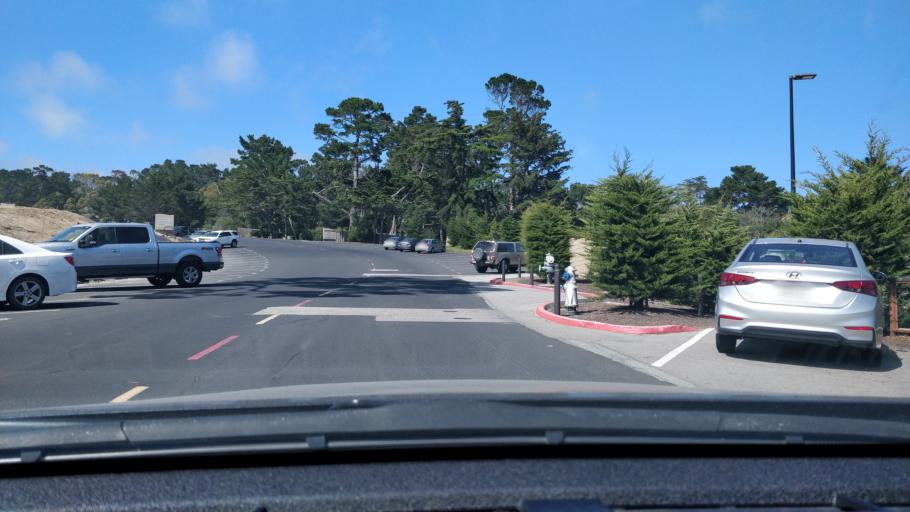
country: US
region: California
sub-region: Monterey County
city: Del Monte Forest
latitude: 36.5709
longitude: -121.9492
